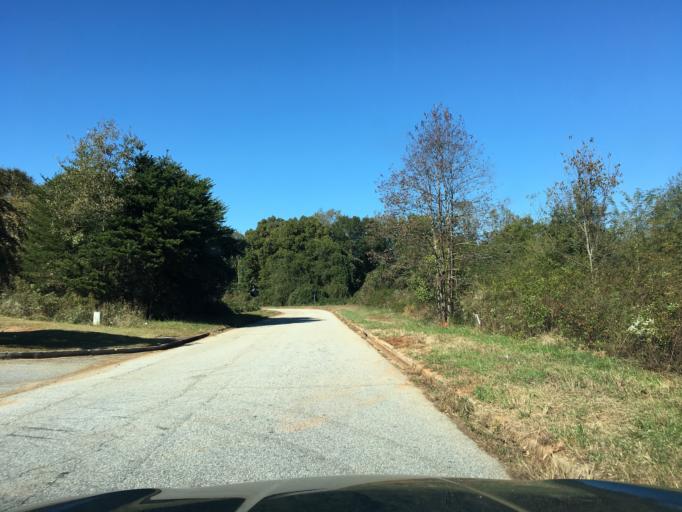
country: US
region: South Carolina
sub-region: Spartanburg County
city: Wellford
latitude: 34.9084
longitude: -82.0884
